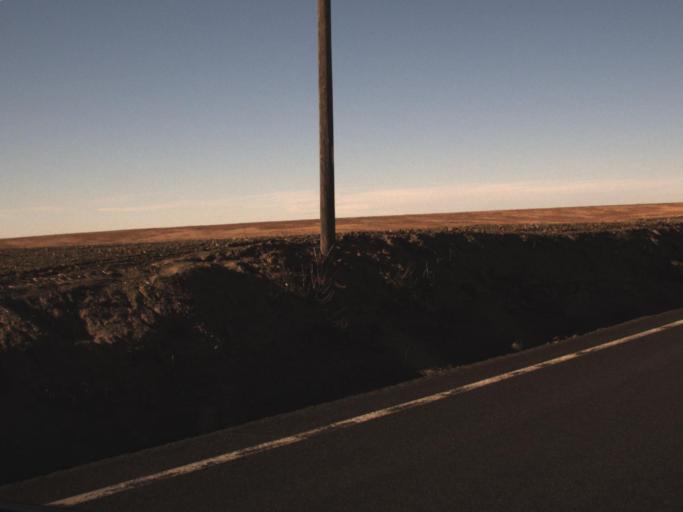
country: US
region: Washington
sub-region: Adams County
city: Ritzville
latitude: 47.0165
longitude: -118.3508
